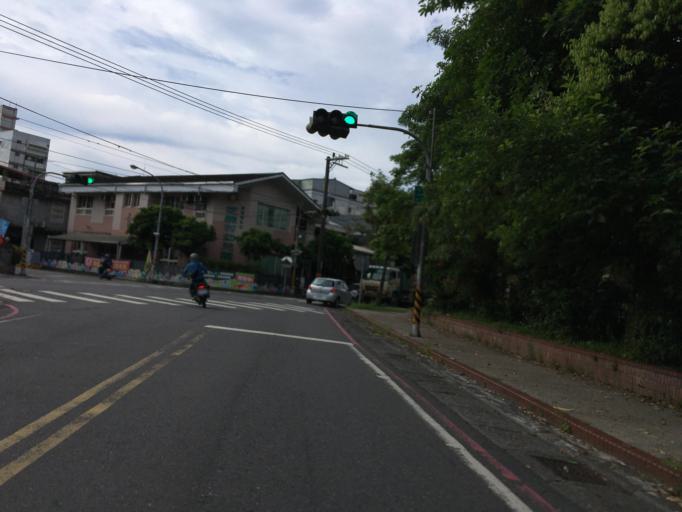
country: TW
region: Taiwan
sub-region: Yilan
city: Yilan
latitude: 24.6830
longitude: 121.7684
